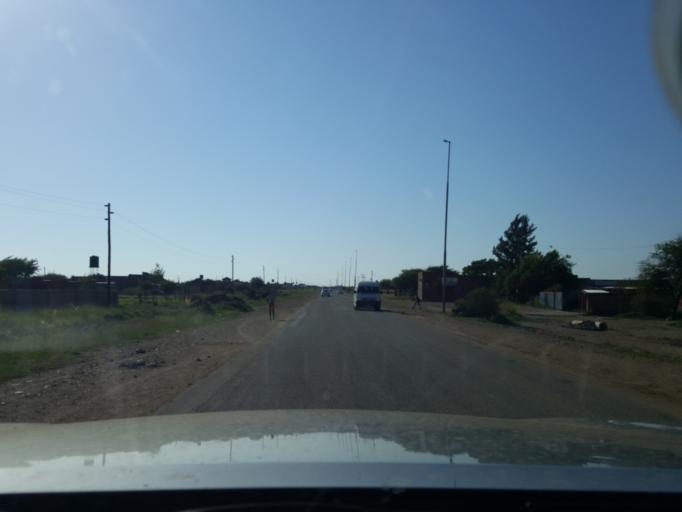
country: ZA
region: North-West
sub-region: Ngaka Modiri Molema District Municipality
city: Mmabatho
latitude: -25.8343
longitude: 25.6626
